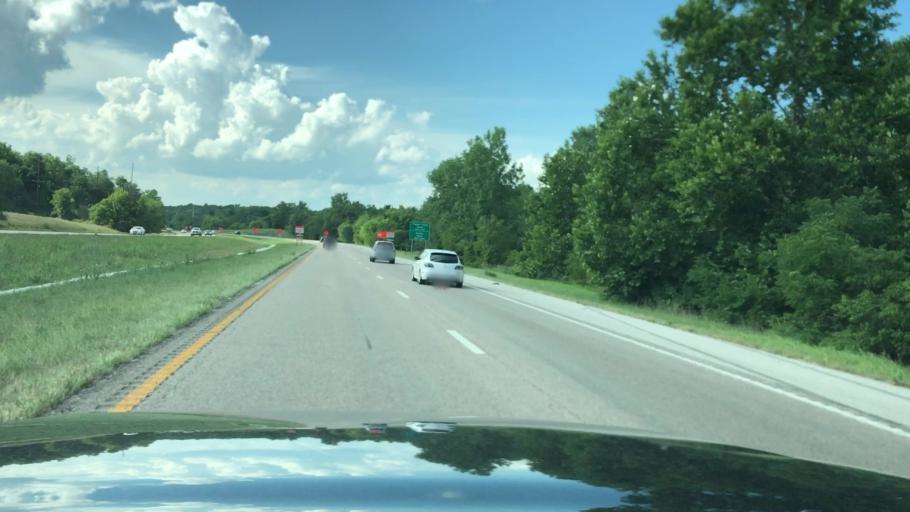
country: US
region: Missouri
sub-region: Saint Charles County
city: Wentzville
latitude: 38.8378
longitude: -90.8574
